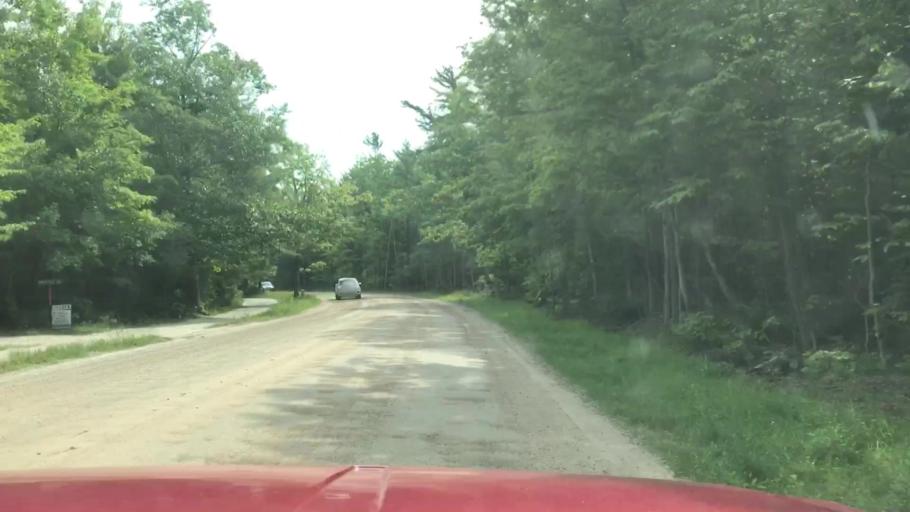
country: US
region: Michigan
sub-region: Charlevoix County
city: Charlevoix
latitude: 45.7470
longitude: -85.5350
